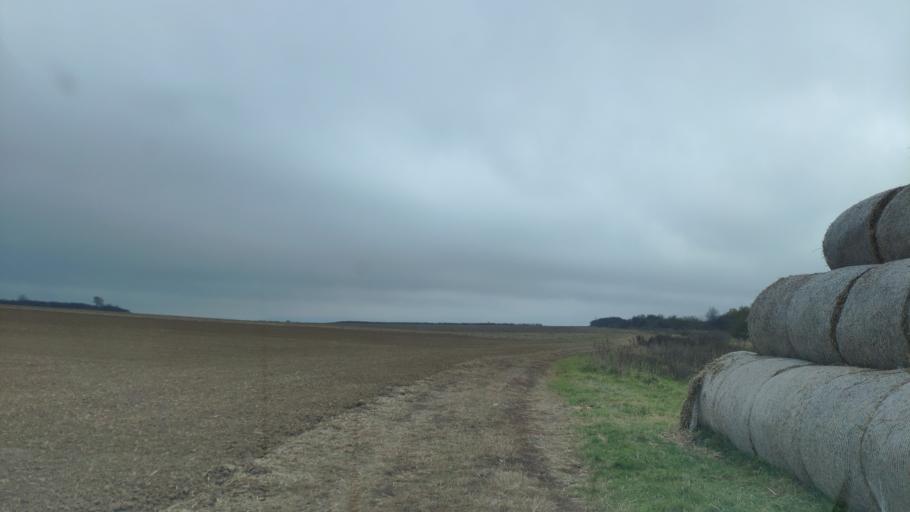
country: SK
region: Presovsky
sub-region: Okres Presov
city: Presov
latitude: 49.0166
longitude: 21.2054
